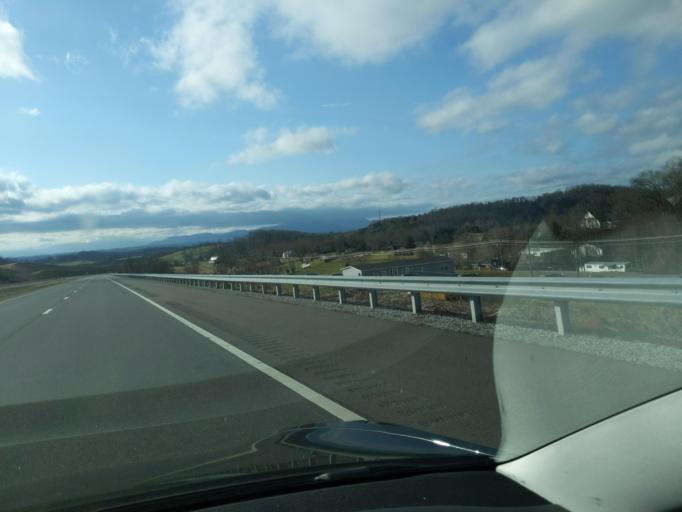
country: US
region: Tennessee
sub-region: Jefferson County
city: White Pine
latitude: 36.1338
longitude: -83.3382
